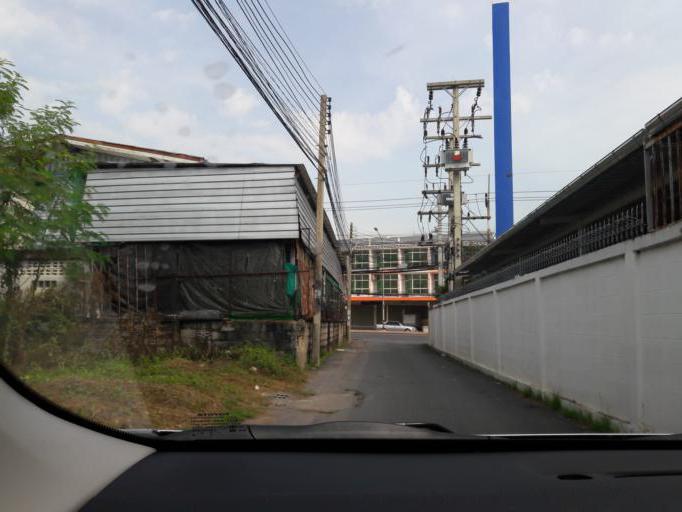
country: TH
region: Ang Thong
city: Ang Thong
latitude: 14.6005
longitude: 100.4352
